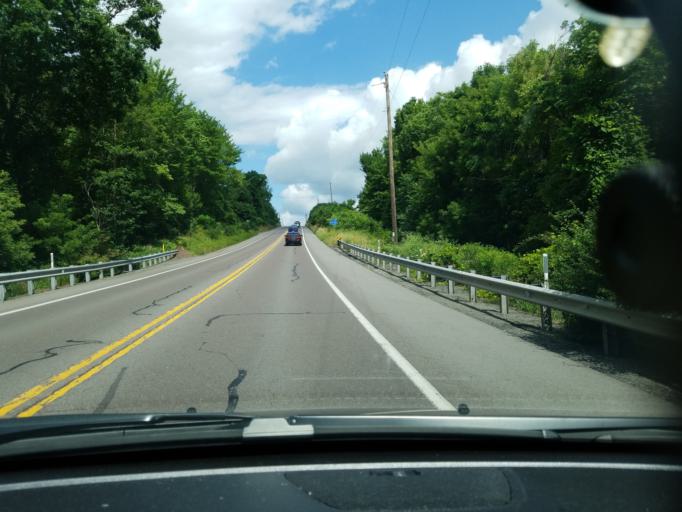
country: US
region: Pennsylvania
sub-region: Northumberland County
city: Elysburg
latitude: 40.8357
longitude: -76.5117
